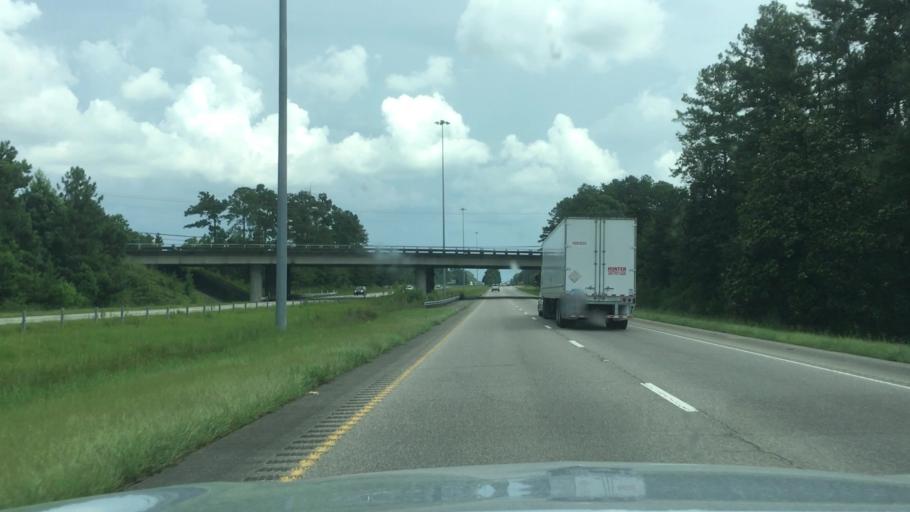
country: US
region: Mississippi
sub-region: Pearl River County
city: Picayune
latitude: 30.5419
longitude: -89.6503
